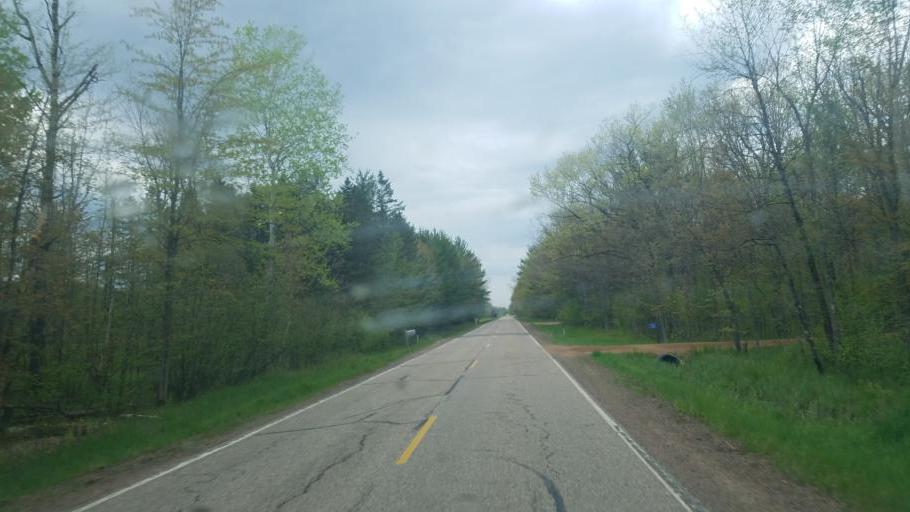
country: US
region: Wisconsin
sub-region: Wood County
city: Marshfield
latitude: 44.5126
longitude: -90.2883
